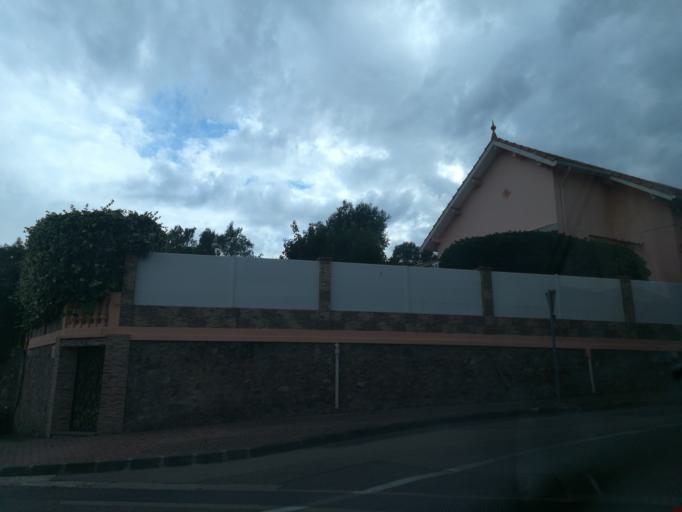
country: FR
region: Languedoc-Roussillon
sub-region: Departement des Pyrenees-Orientales
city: el Volo
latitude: 42.5223
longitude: 2.8323
